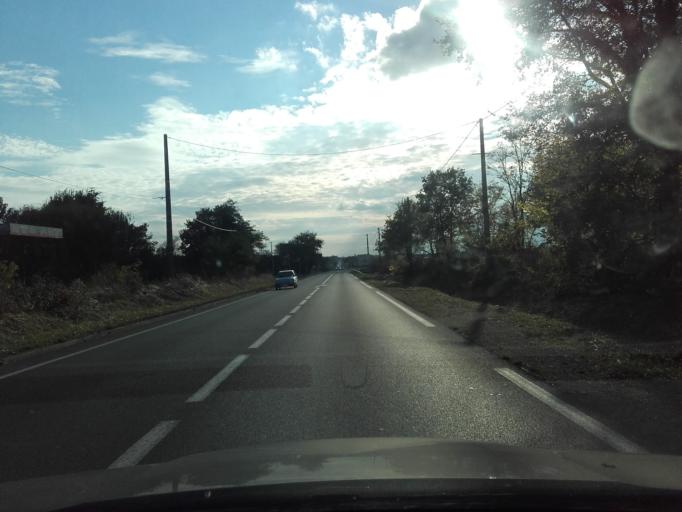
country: FR
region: Centre
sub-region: Departement d'Indre-et-Loire
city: Parcay-Meslay
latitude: 47.4665
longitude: 0.7477
